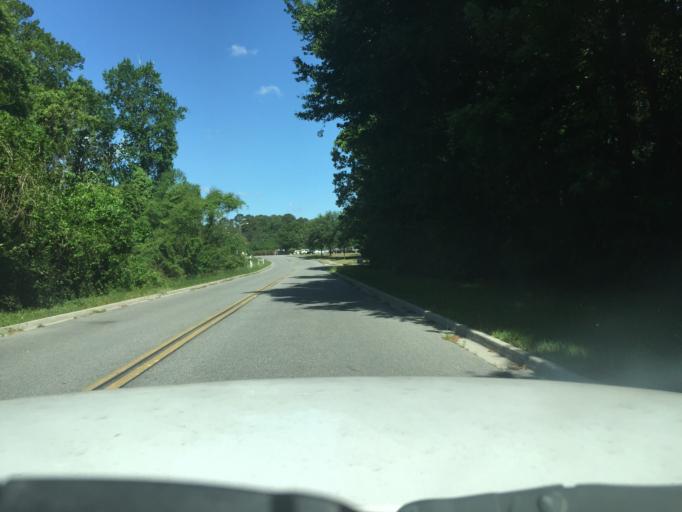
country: US
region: Georgia
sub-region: Chatham County
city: Isle of Hope
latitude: 32.0037
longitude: -81.0984
